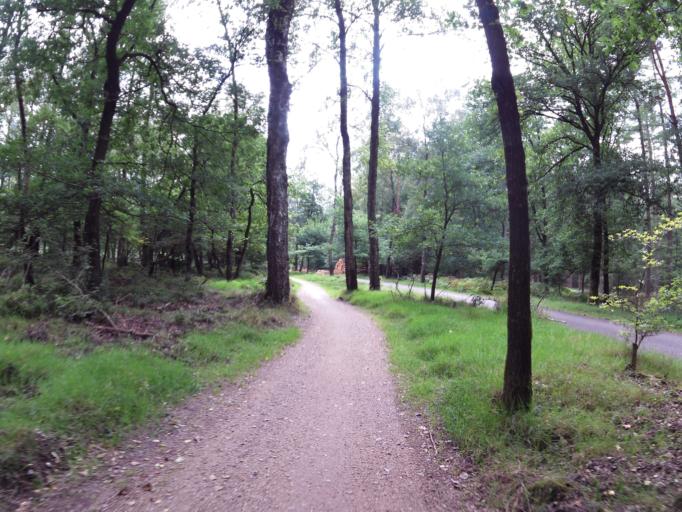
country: NL
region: Gelderland
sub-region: Gemeente Apeldoorn
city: Loenen
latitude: 52.0989
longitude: 5.9949
